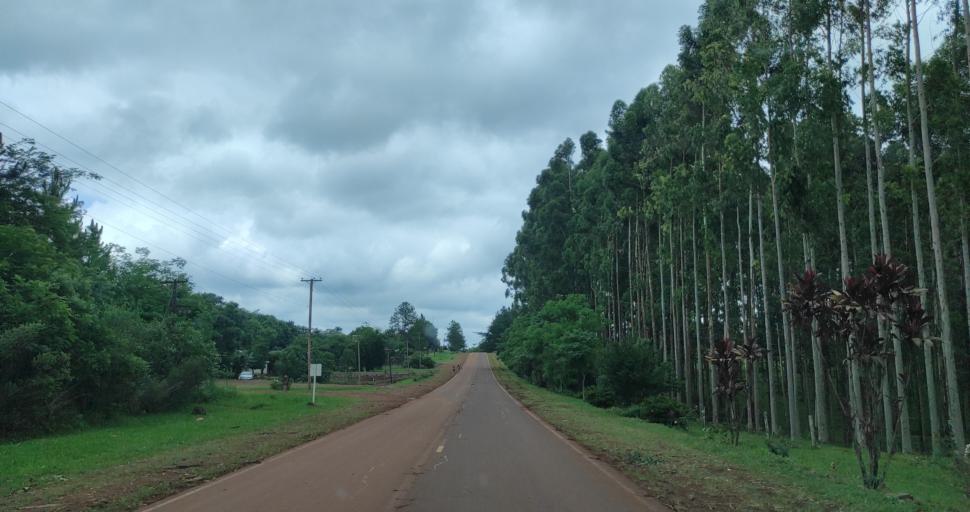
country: AR
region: Misiones
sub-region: Departamento de Veinticinco de Mayo
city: Veinticinco de Mayo
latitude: -27.3905
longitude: -54.7481
